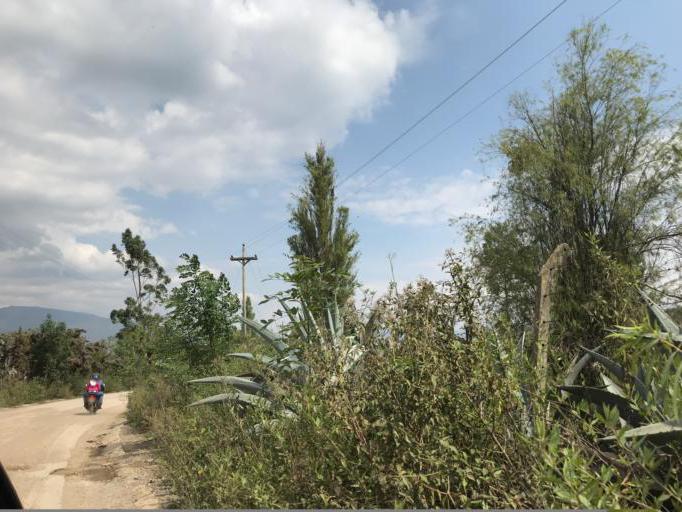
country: CO
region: Boyaca
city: Villa de Leiva
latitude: 5.6603
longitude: -73.5825
